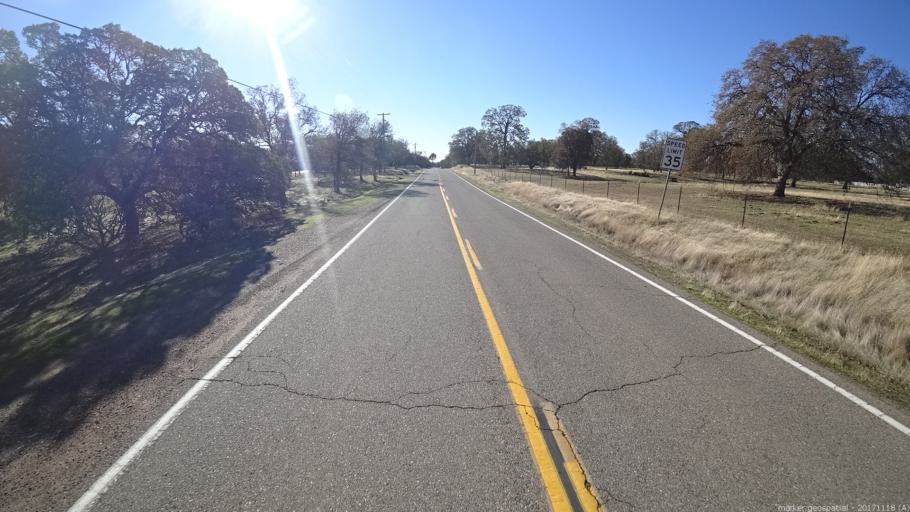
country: US
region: California
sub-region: Shasta County
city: Cottonwood
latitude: 40.3980
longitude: -122.3145
